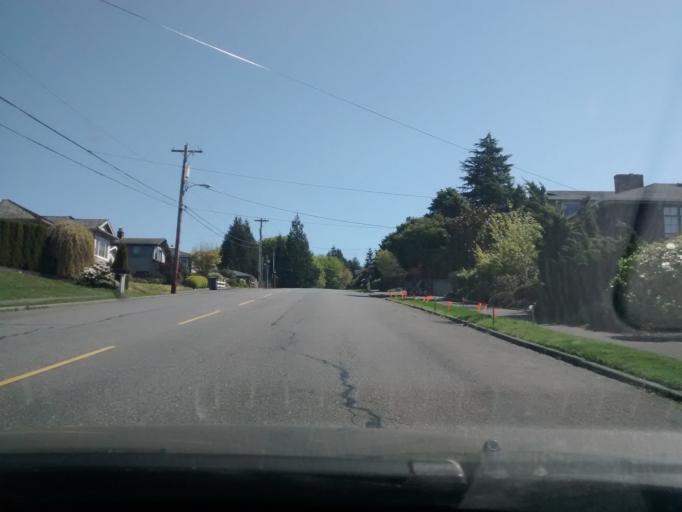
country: US
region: Washington
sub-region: Snohomish County
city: Edmonds
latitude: 47.8097
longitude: -122.3690
